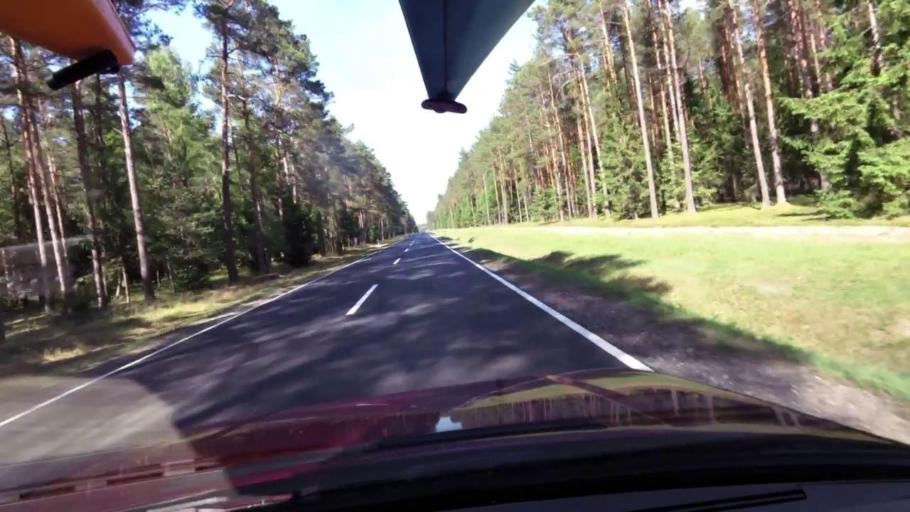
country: PL
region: Pomeranian Voivodeship
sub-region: Powiat bytowski
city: Trzebielino
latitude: 54.1370
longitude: 17.0215
